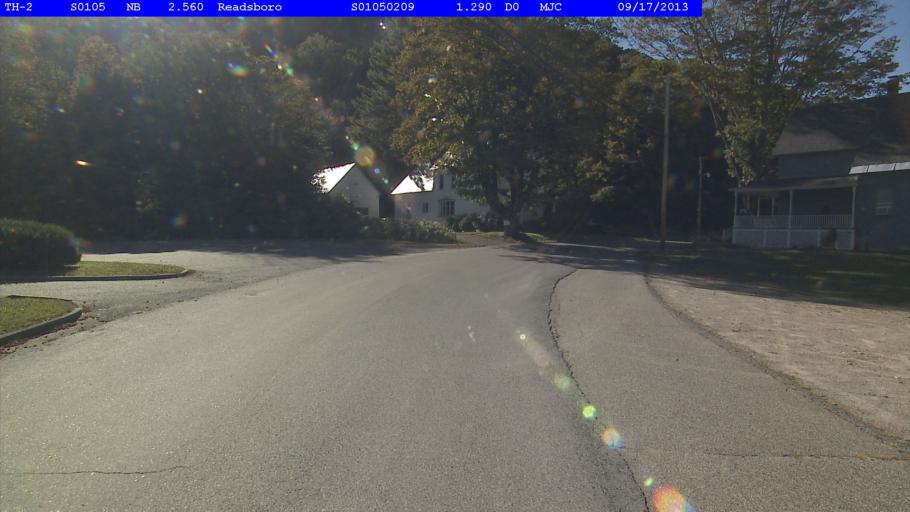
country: US
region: Massachusetts
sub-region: Franklin County
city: Charlemont
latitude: 42.7680
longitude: -72.9464
